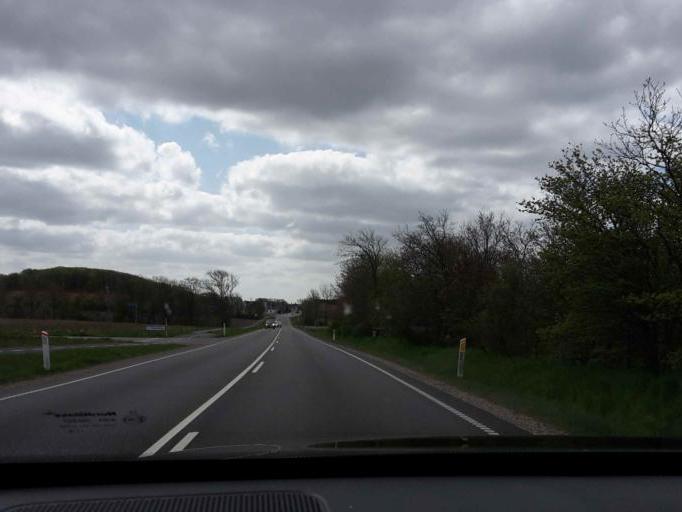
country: DK
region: South Denmark
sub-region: Varde Kommune
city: Olgod
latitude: 55.7256
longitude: 8.6128
